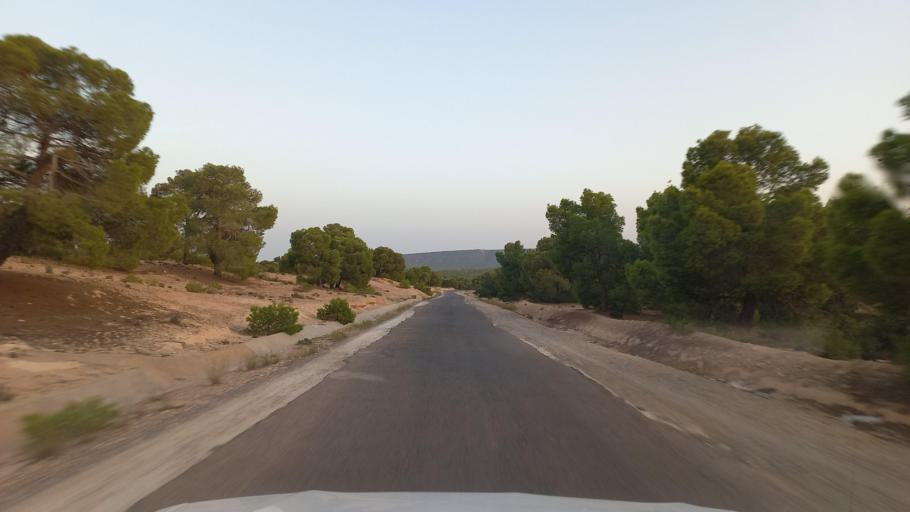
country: TN
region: Al Qasrayn
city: Sbiba
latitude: 35.4199
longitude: 8.9243
